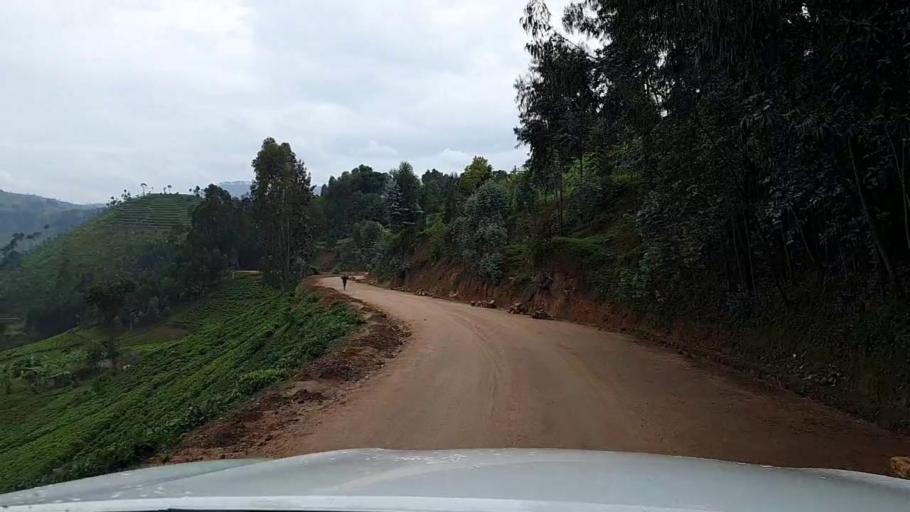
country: RW
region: Southern Province
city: Nzega
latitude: -2.4604
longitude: 29.4665
